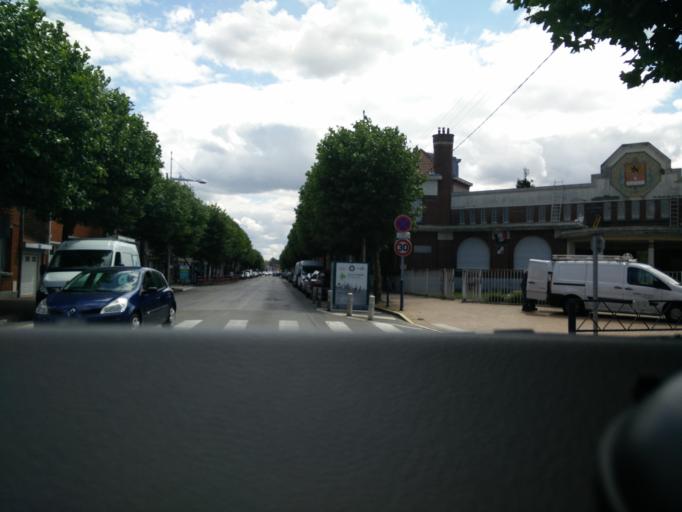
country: FR
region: Nord-Pas-de-Calais
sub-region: Departement du Nord
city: Coudekerque-Branche
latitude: 51.0470
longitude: 2.4026
